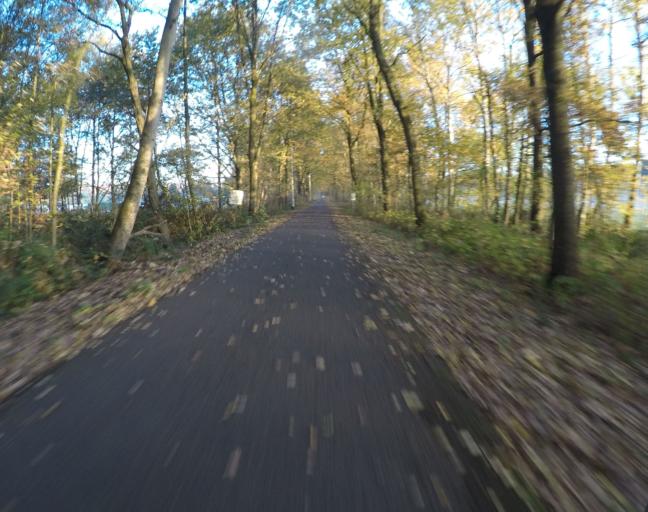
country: BE
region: Flanders
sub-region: Provincie Antwerpen
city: Hulshout
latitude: 51.0769
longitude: 4.8252
